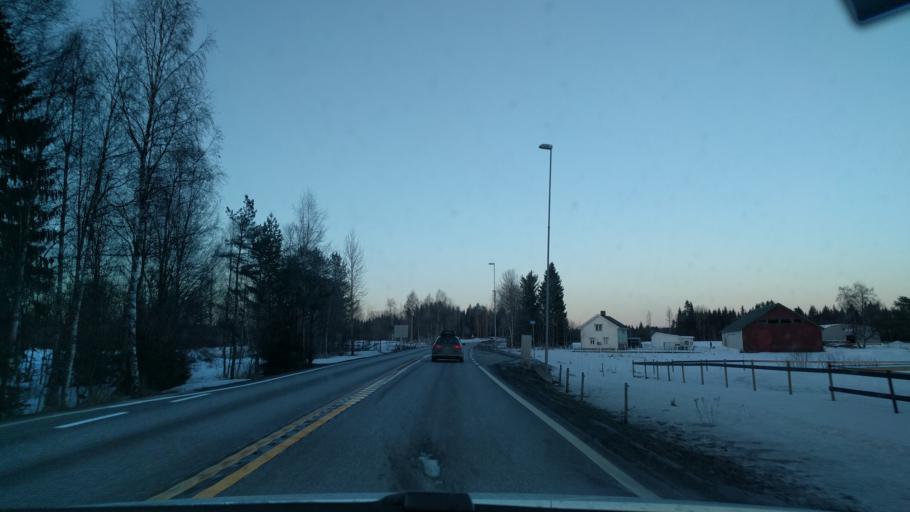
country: NO
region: Hedmark
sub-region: Loten
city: Loten
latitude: 60.8637
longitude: 11.4187
